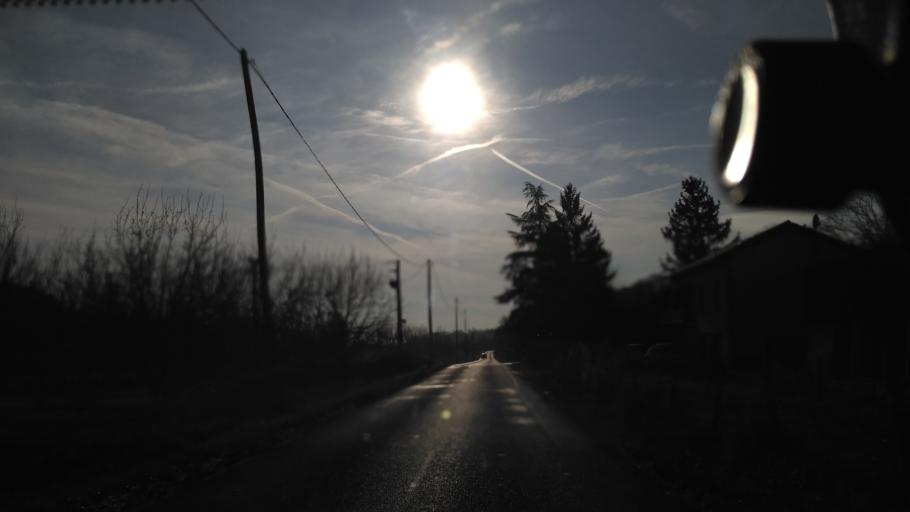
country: FR
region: Rhone-Alpes
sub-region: Departement de la Drome
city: Saint-Paul-les-Romans
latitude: 45.1059
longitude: 5.1424
